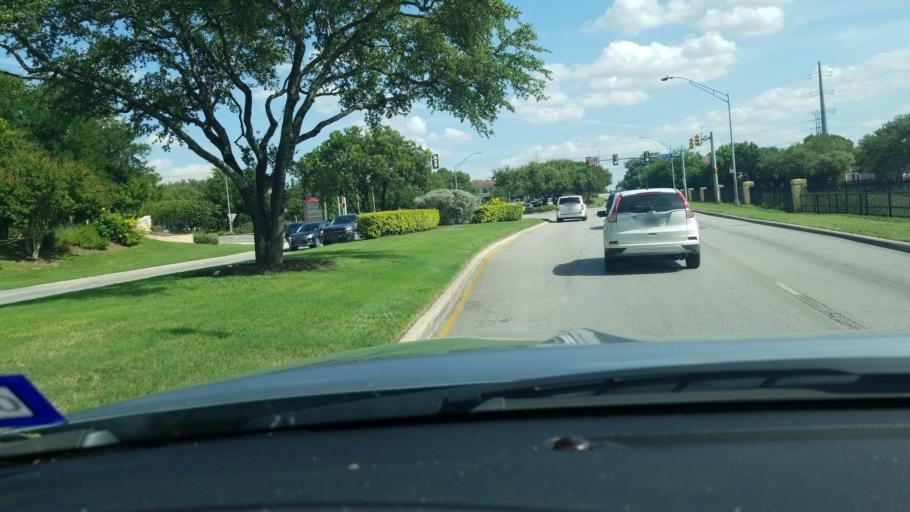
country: US
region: Texas
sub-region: Bexar County
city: Hollywood Park
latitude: 29.6216
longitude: -98.4946
